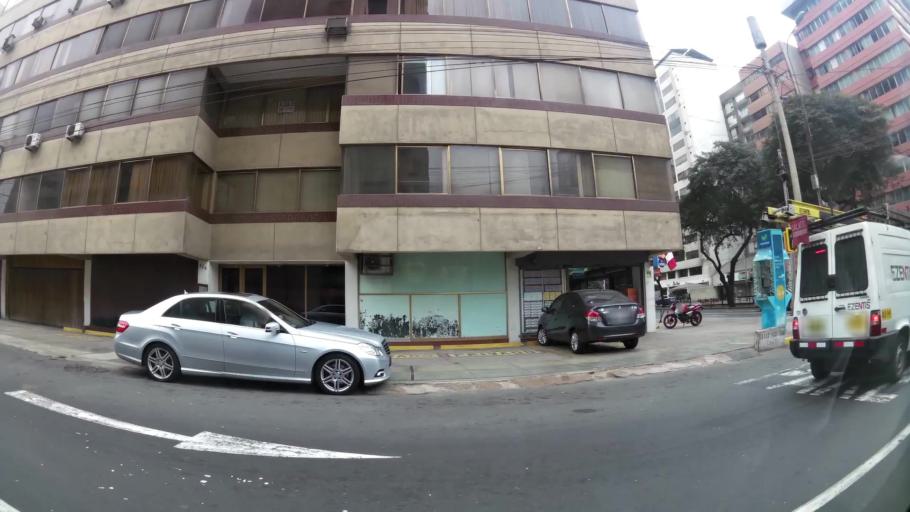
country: PE
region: Lima
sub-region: Lima
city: San Isidro
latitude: -12.1188
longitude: -77.0348
